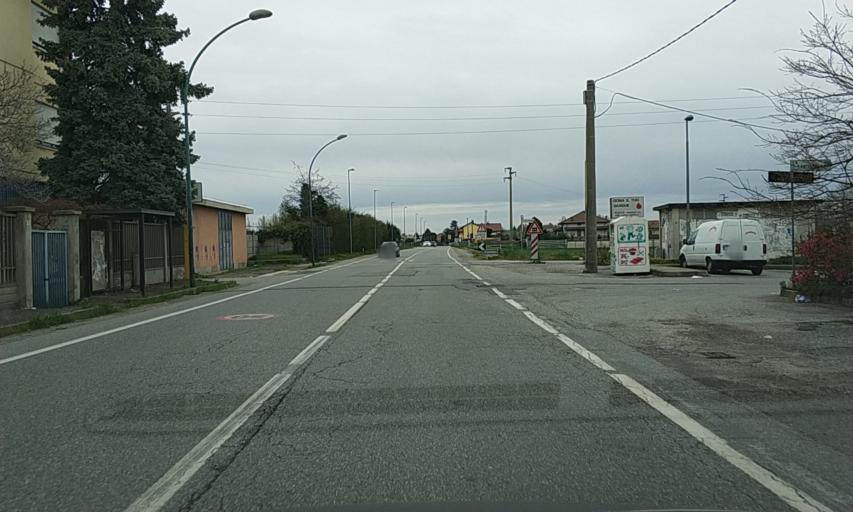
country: IT
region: Piedmont
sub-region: Provincia di Torino
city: Favria
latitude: 45.3315
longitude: 7.7020
